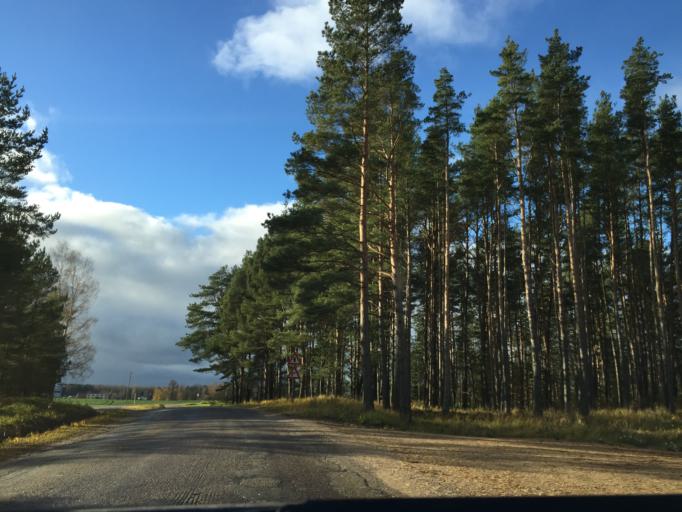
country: LV
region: Kandava
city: Kandava
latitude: 56.9695
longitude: 22.9394
